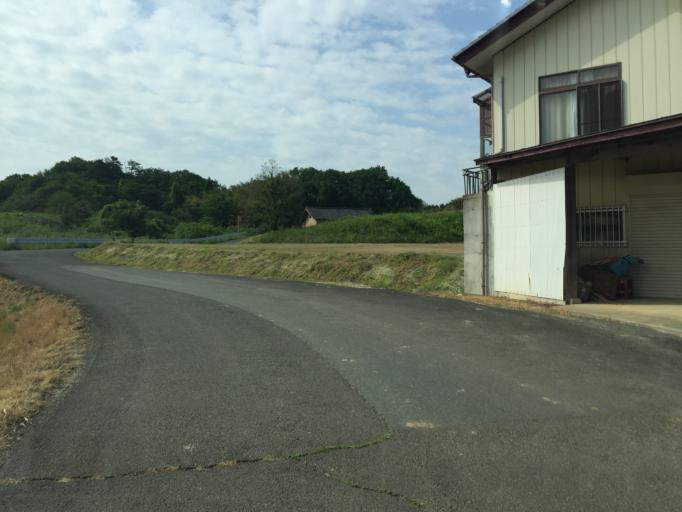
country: JP
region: Fukushima
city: Fukushima-shi
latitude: 37.6730
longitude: 140.4705
